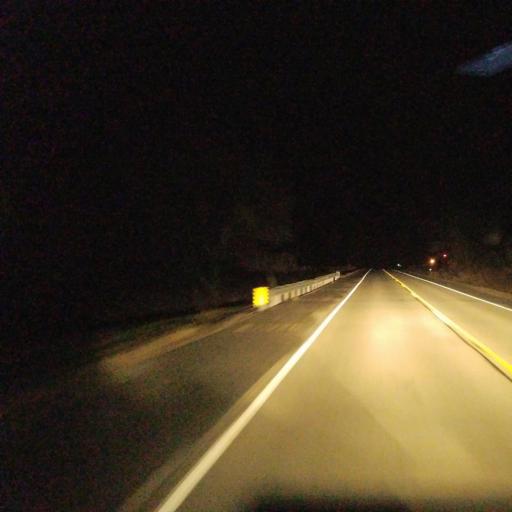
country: US
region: Illinois
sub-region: Knox County
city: Abingdon
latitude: 40.7293
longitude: -90.4236
